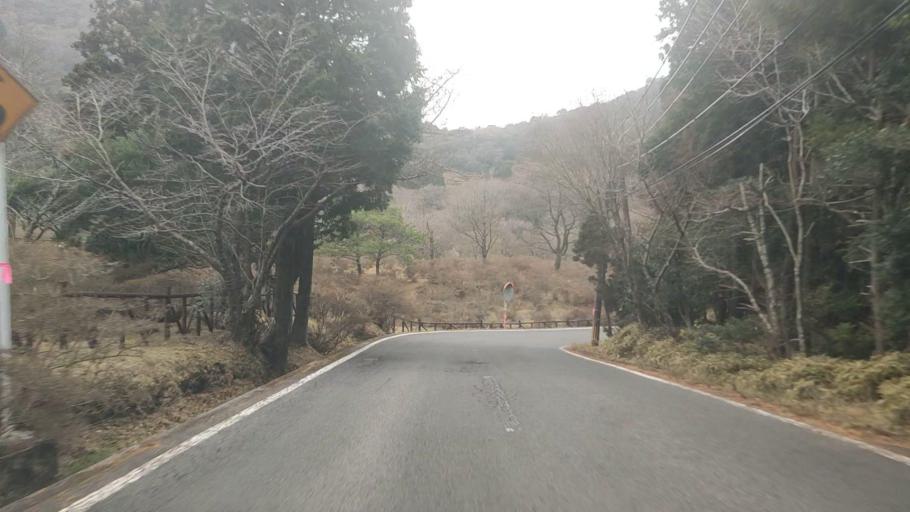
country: JP
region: Nagasaki
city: Shimabara
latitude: 32.7453
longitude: 130.2689
